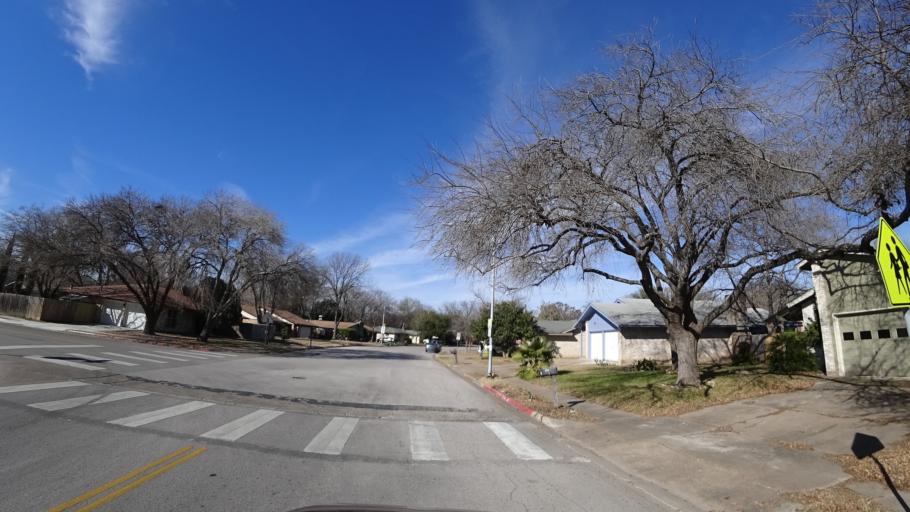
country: US
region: Texas
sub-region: Travis County
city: Wells Branch
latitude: 30.3791
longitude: -97.7044
